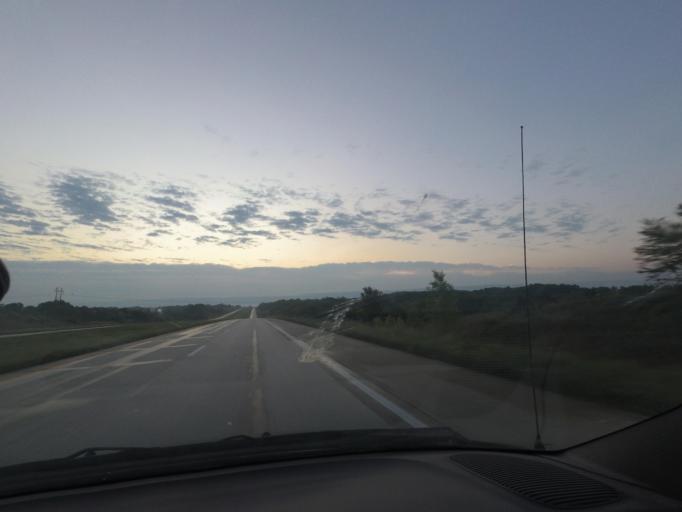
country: US
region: Missouri
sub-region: Macon County
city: Macon
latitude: 39.7591
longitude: -92.6642
